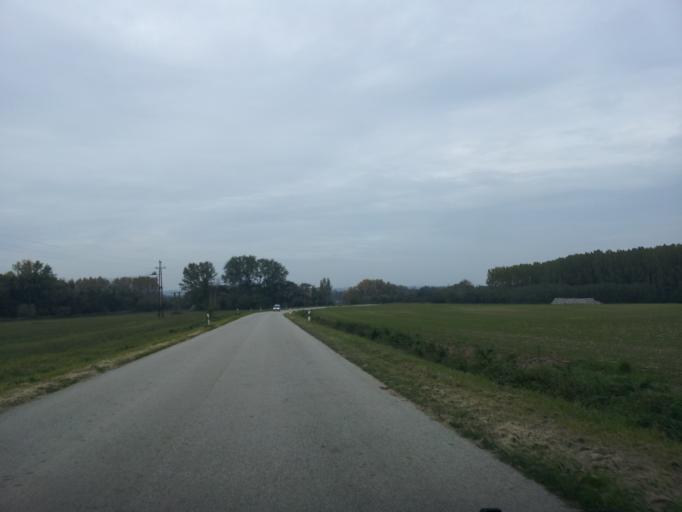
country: HU
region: Gyor-Moson-Sopron
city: Bakonyszentlaszlo
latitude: 47.4042
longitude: 17.7992
